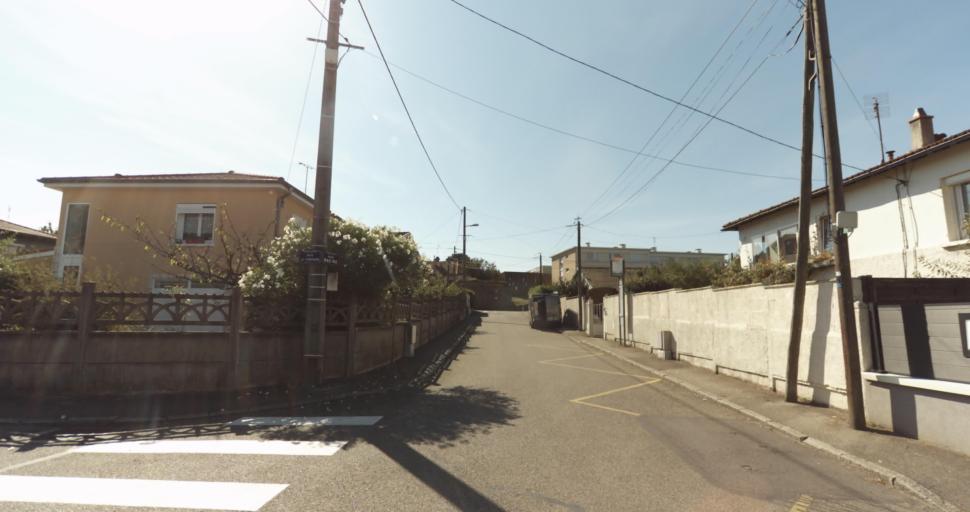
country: FR
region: Rhone-Alpes
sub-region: Departement du Rhone
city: Fleurieu-sur-Saone
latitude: 45.8716
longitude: 4.8426
